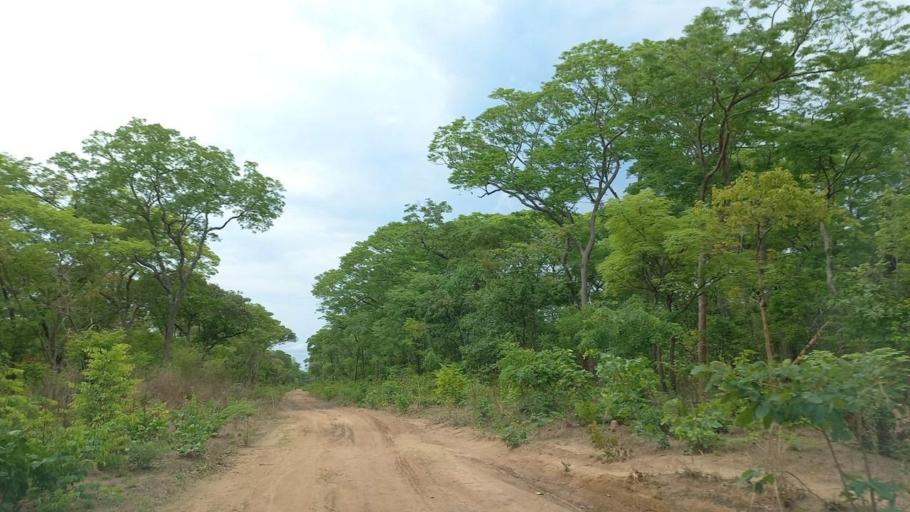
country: ZM
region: North-Western
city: Kalengwa
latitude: -13.5452
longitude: 24.9766
